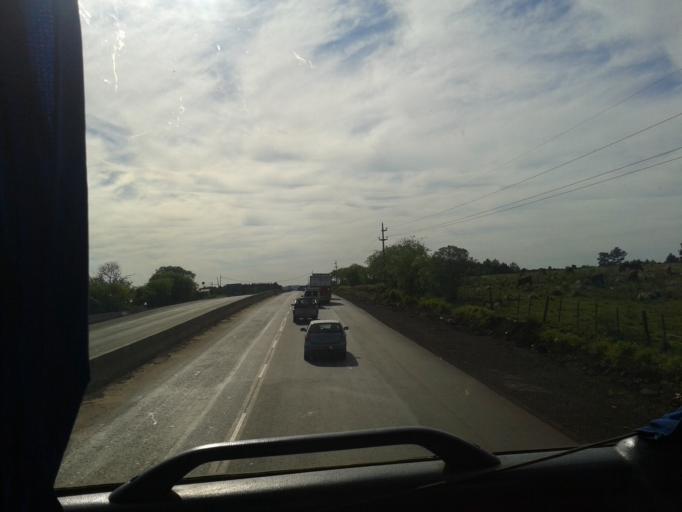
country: AR
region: Misiones
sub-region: Departamento de Candelaria
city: Candelaria
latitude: -27.4625
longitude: -55.6931
